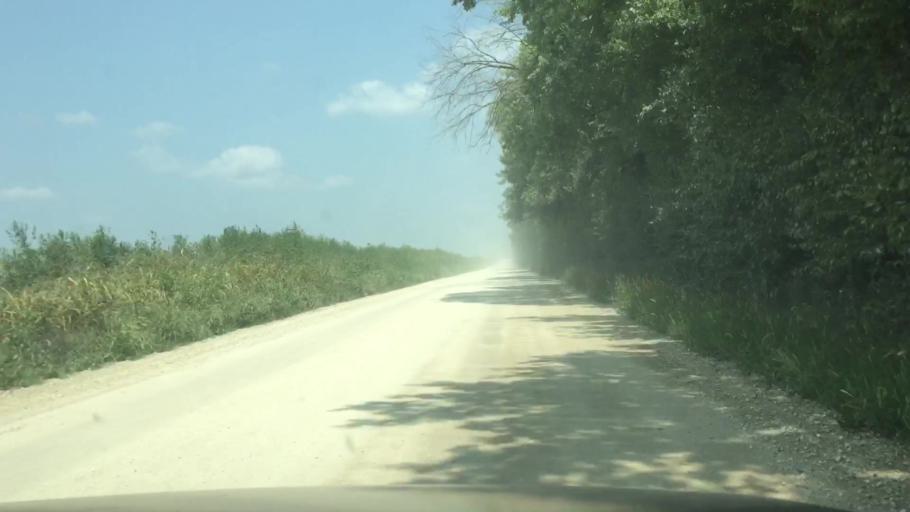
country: US
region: Kansas
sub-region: Allen County
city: Humboldt
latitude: 37.8273
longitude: -95.4093
